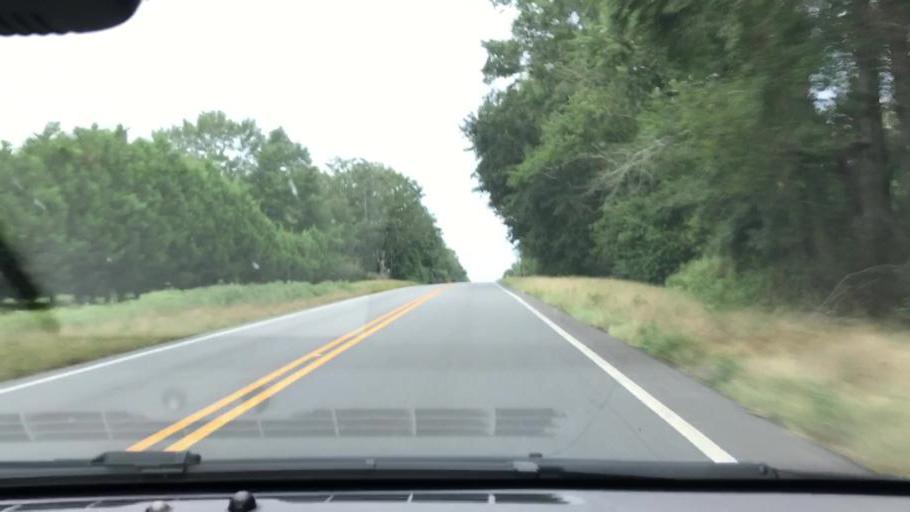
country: US
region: Alabama
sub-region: Houston County
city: Webb
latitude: 31.2742
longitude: -85.1565
